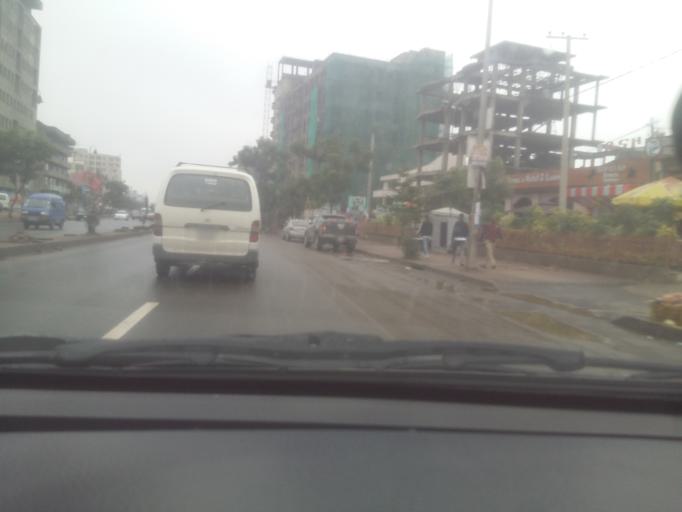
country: ET
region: Adis Abeba
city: Addis Ababa
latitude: 8.9493
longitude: 38.7208
